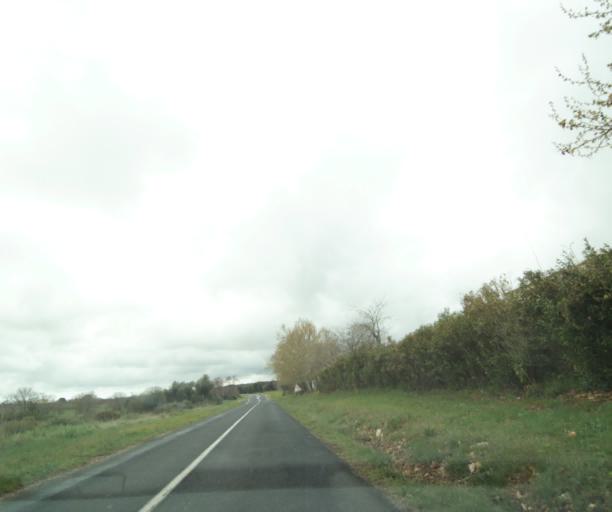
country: FR
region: Languedoc-Roussillon
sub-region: Departement de l'Herault
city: Cournonsec
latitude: 43.5424
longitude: 3.7019
